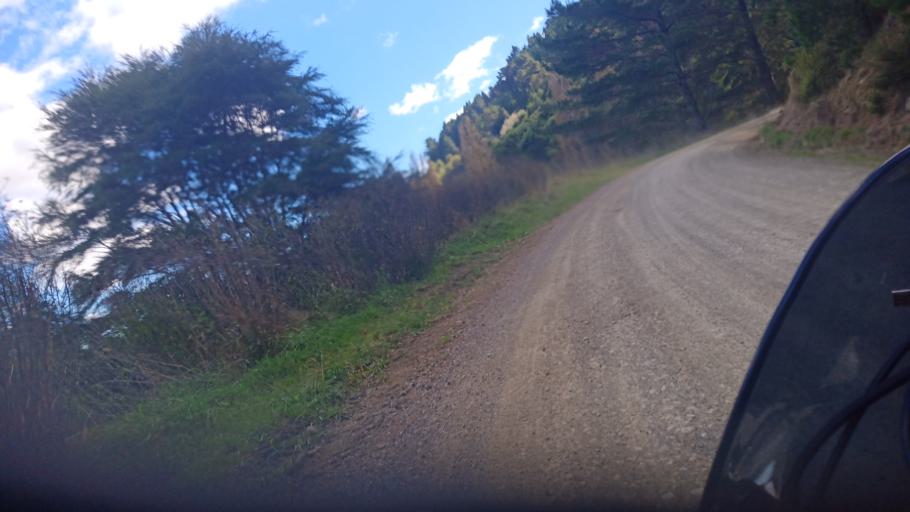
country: NZ
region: Gisborne
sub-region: Gisborne District
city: Gisborne
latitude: -38.4113
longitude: 177.6871
